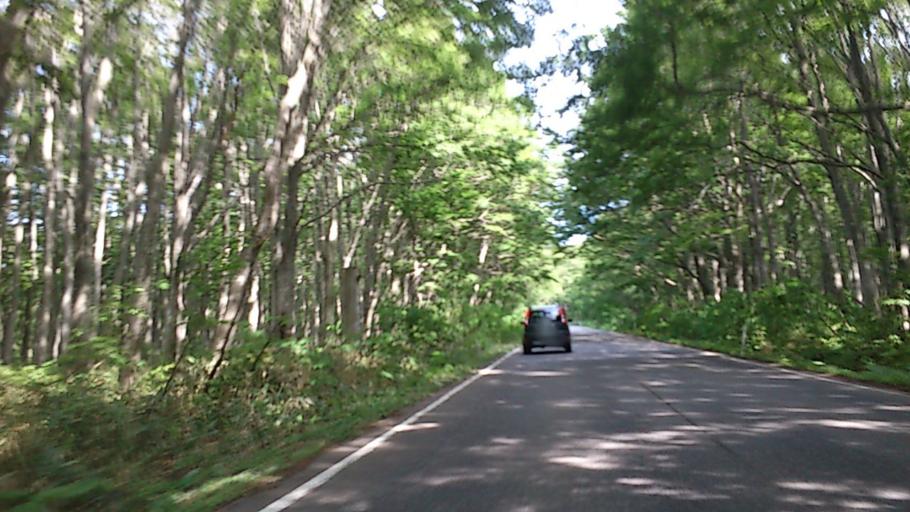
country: JP
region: Aomori
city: Aomori Shi
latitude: 40.6986
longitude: 140.8359
